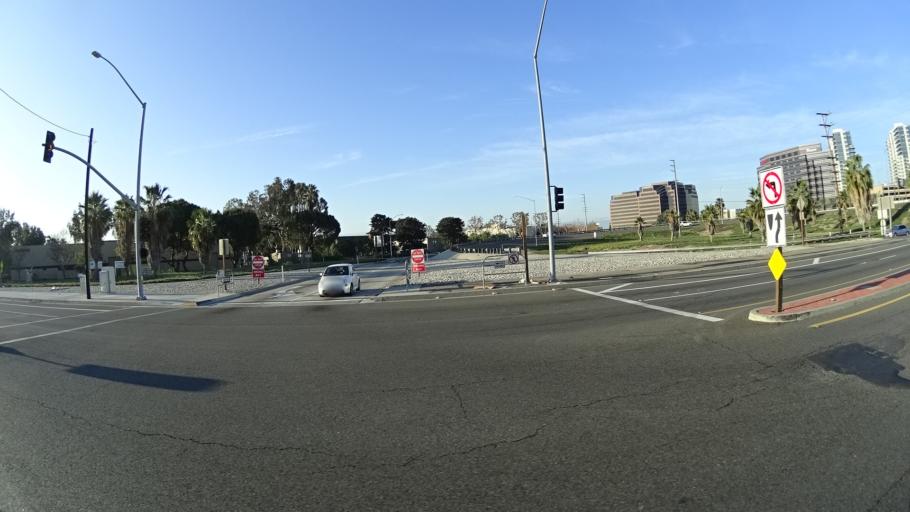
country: US
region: California
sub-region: Orange County
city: Irvine
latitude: 33.6978
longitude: -117.8602
